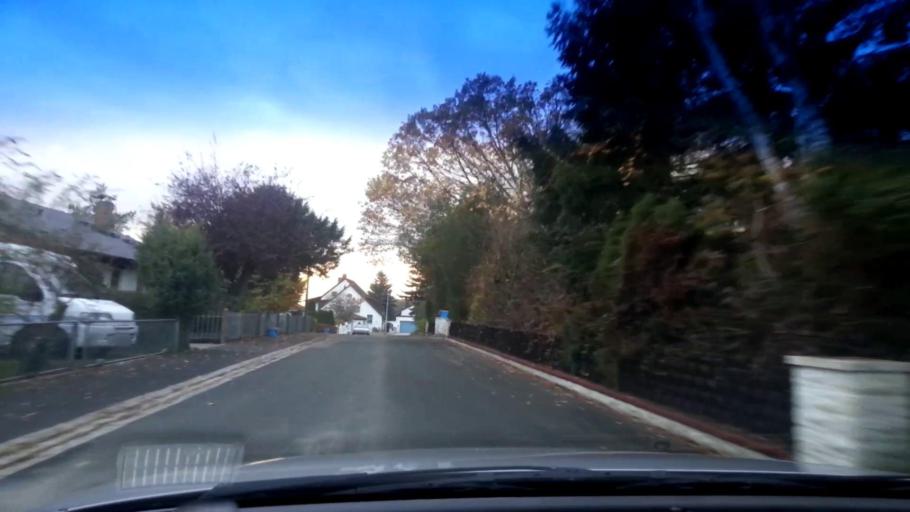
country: DE
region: Bavaria
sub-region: Upper Franconia
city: Memmelsdorf
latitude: 49.9426
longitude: 10.9522
